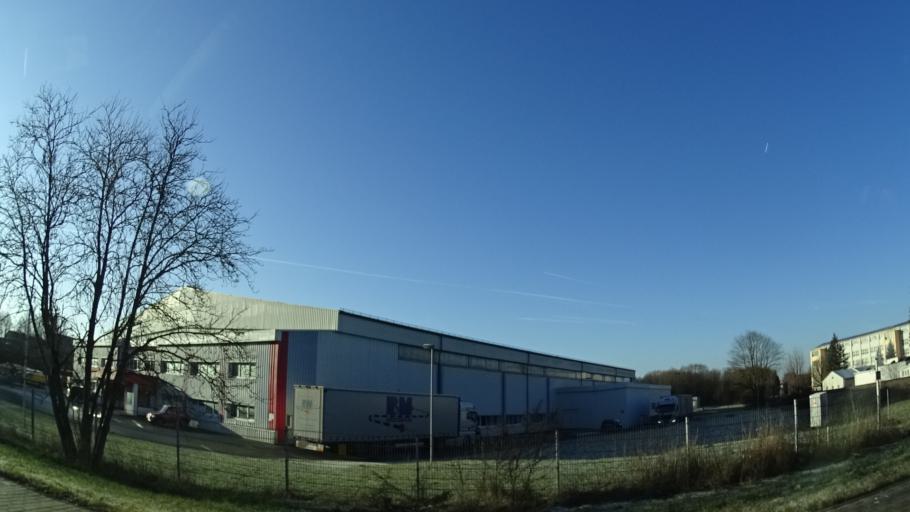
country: DE
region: Bavaria
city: Foritz
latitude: 50.3529
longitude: 11.2094
